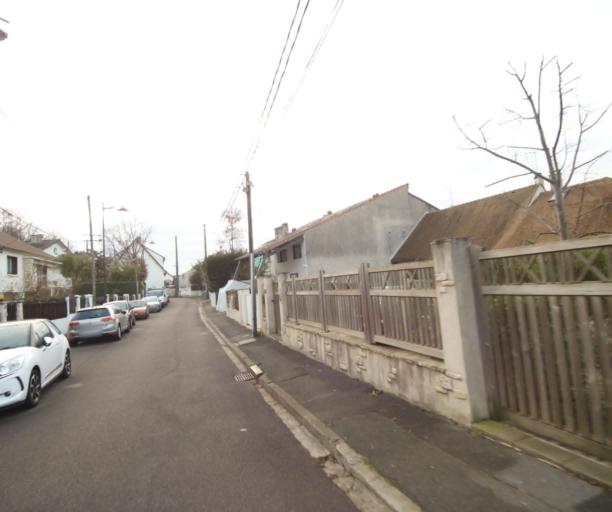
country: FR
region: Ile-de-France
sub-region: Departement des Hauts-de-Seine
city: Suresnes
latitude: 48.8713
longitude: 2.2093
